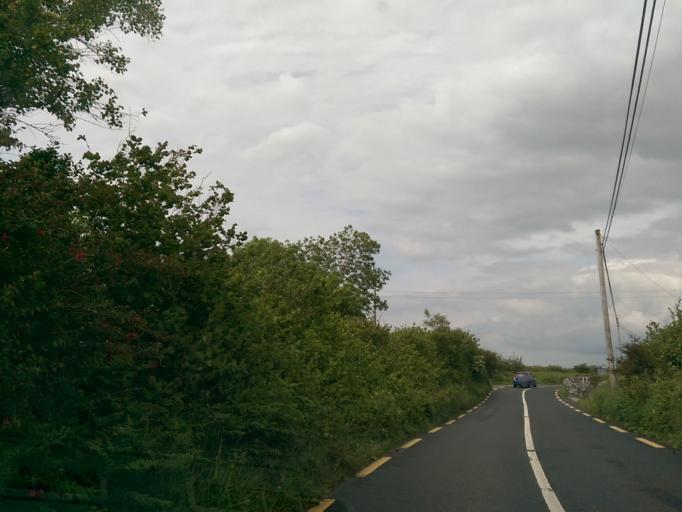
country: IE
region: Connaught
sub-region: County Galway
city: Bearna
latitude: 53.0635
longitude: -9.1917
